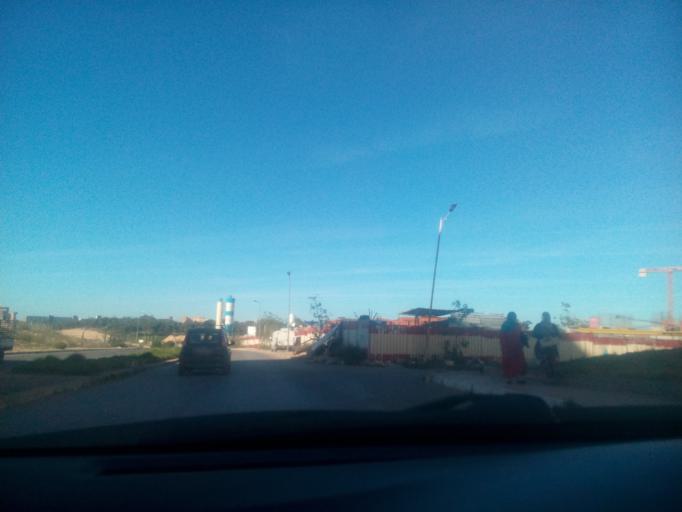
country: DZ
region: Oran
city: Bir el Djir
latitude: 35.7541
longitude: -0.5570
